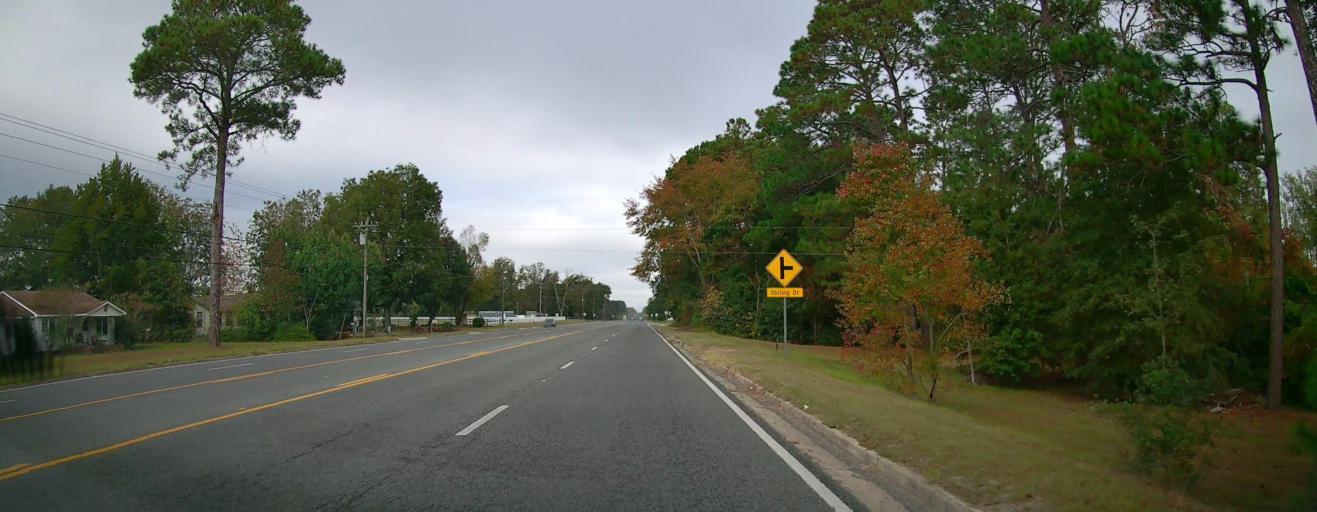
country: US
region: Georgia
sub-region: Tift County
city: Unionville
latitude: 31.4019
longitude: -83.5359
